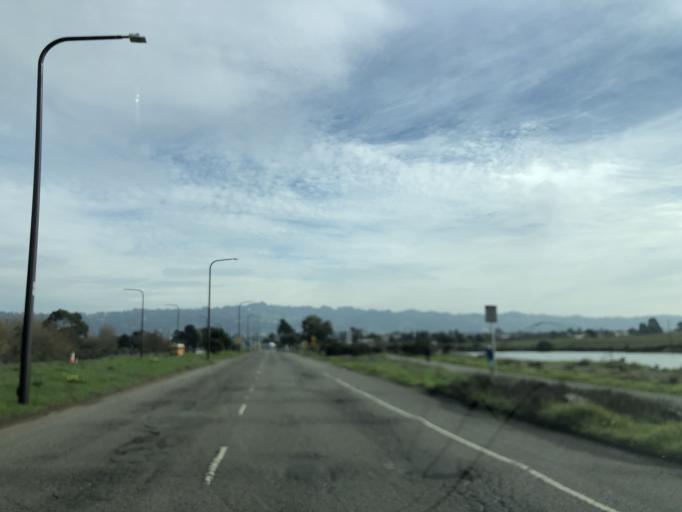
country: US
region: California
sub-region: Alameda County
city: Albany
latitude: 37.8655
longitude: -122.3092
